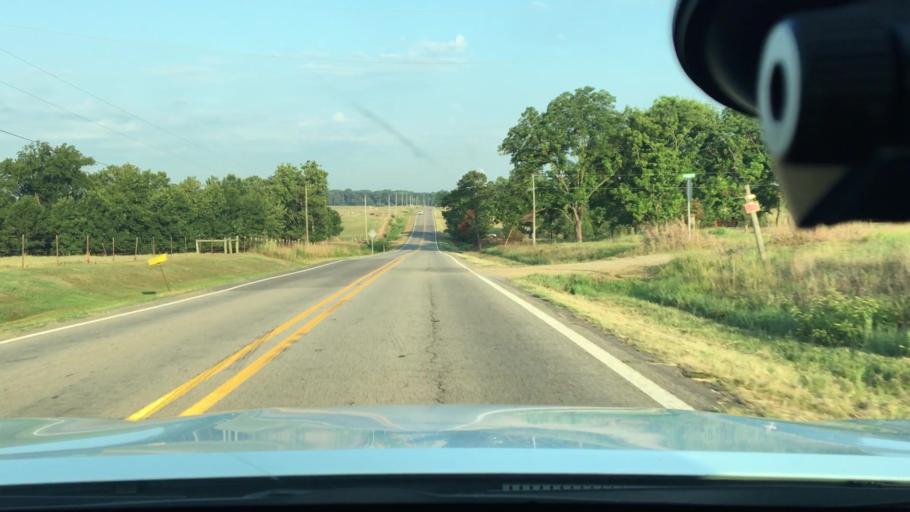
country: US
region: Arkansas
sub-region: Johnson County
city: Clarksville
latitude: 35.3790
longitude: -93.5454
